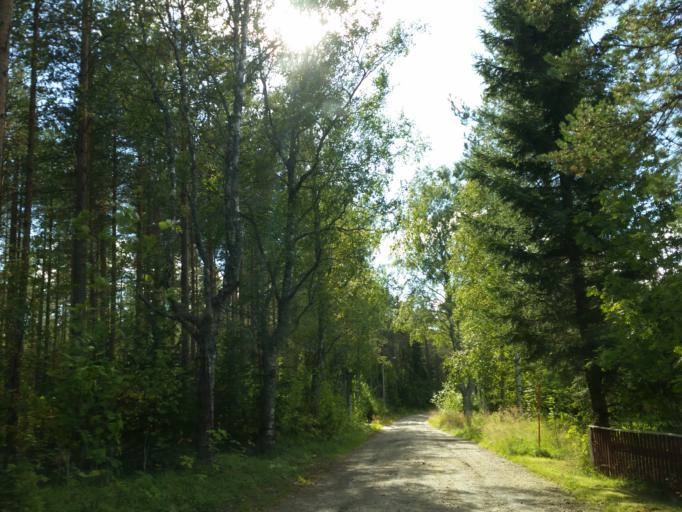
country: SE
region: Vaesterbotten
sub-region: Robertsfors Kommun
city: Robertsfors
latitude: 64.0473
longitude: 20.8718
